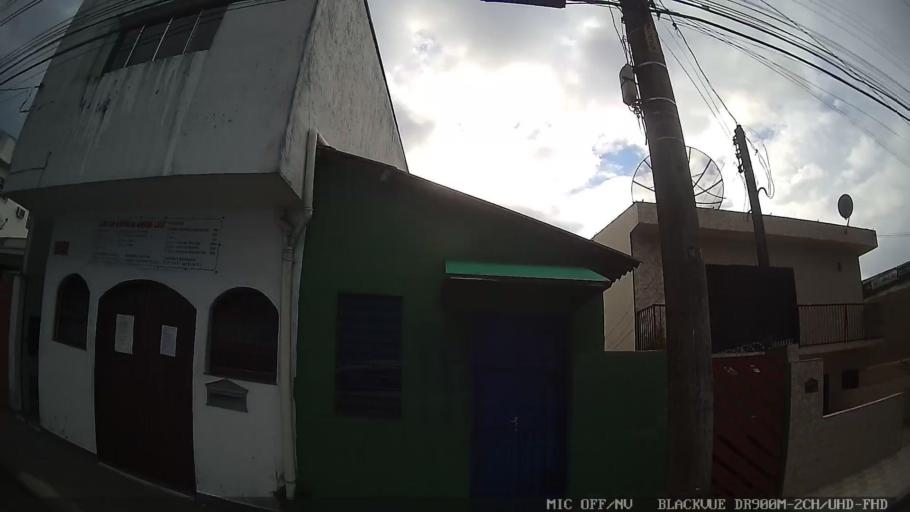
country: BR
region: Sao Paulo
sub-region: Itanhaem
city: Itanhaem
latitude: -24.1796
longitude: -46.7865
